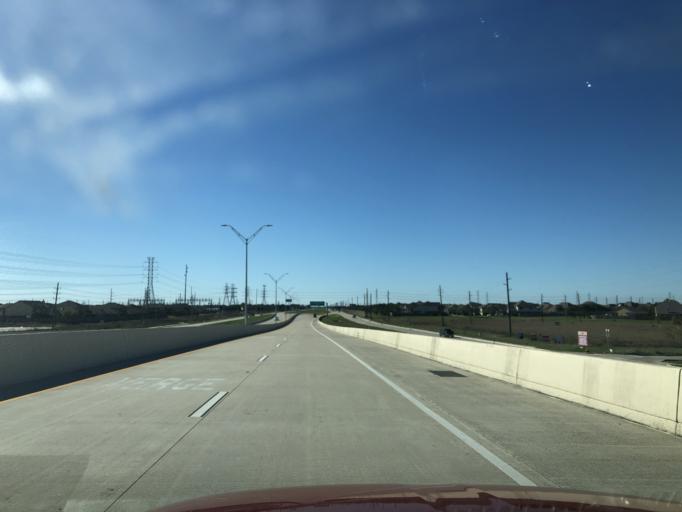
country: US
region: Texas
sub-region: Fort Bend County
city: Cinco Ranch
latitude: 29.6974
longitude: -95.8145
